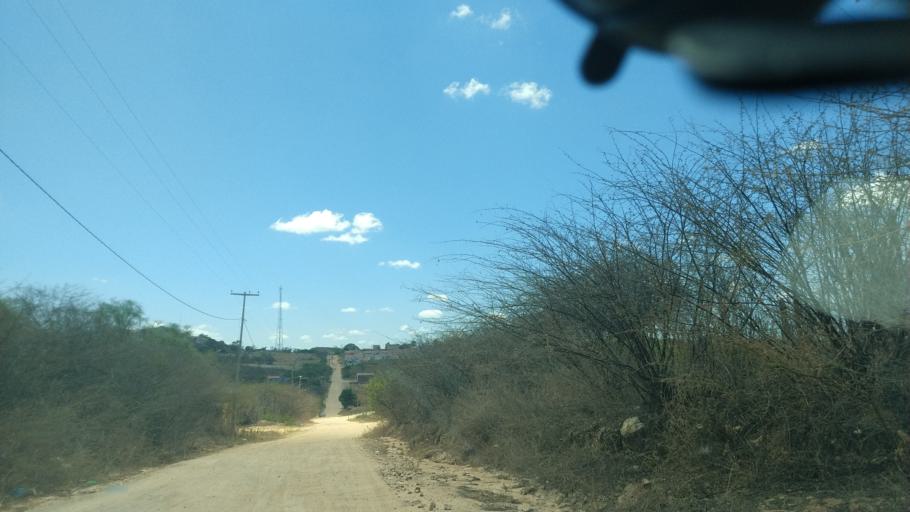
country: BR
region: Rio Grande do Norte
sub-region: Cerro Cora
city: Cerro Cora
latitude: -6.0303
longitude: -36.3408
